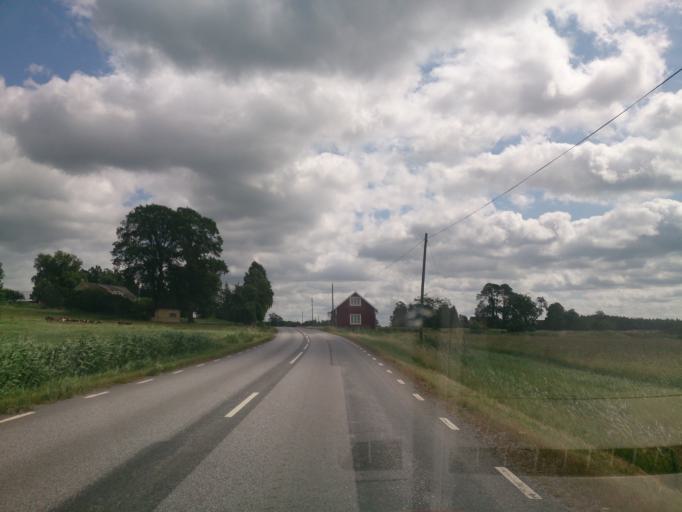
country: SE
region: OEstergoetland
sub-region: Soderkopings Kommun
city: Soederkoeping
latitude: 58.5260
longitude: 16.4351
